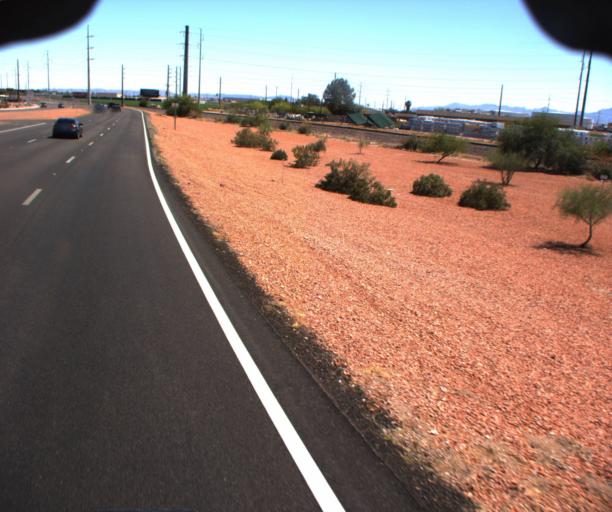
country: US
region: Arizona
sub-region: Maricopa County
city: Peoria
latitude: 33.5620
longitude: -112.2132
